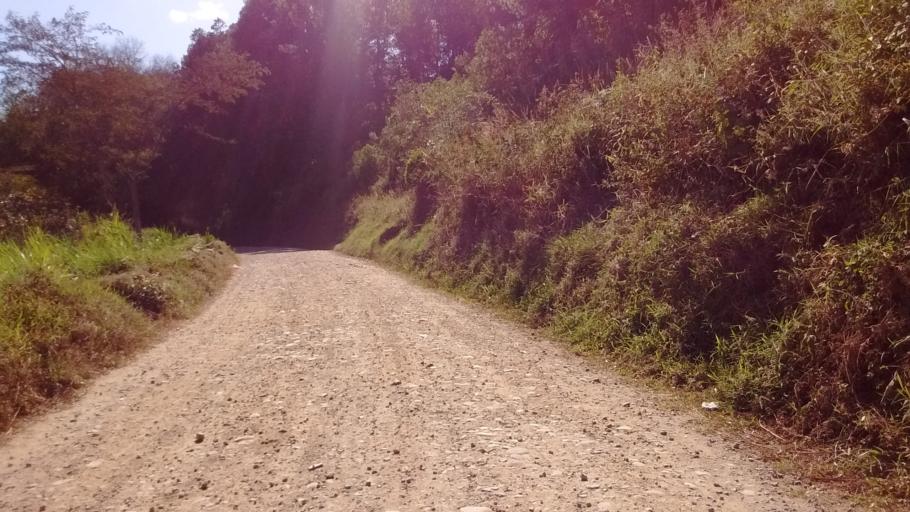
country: CO
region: Cauca
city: Popayan
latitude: 2.4664
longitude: -76.5764
